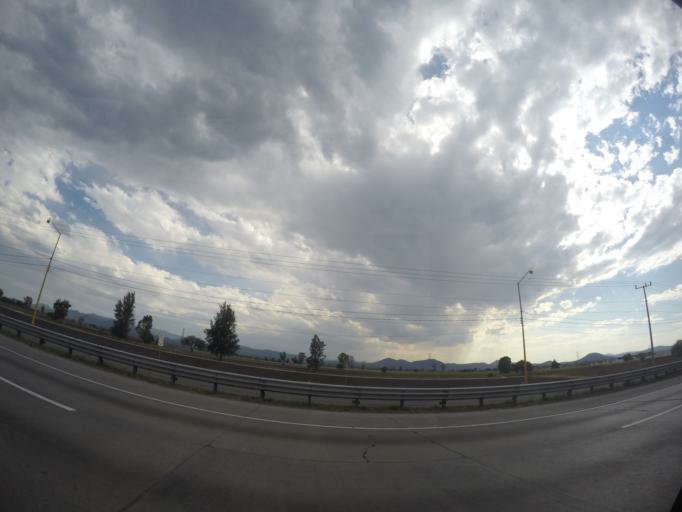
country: MX
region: Queretaro
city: La Estancia
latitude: 20.4239
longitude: -100.0528
